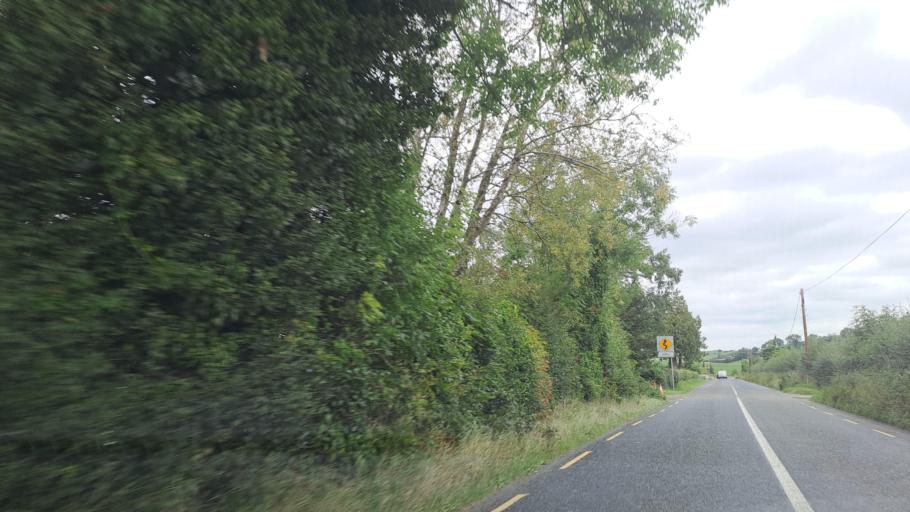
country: IE
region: Ulster
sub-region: An Cabhan
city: Bailieborough
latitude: 53.9680
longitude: -6.9157
